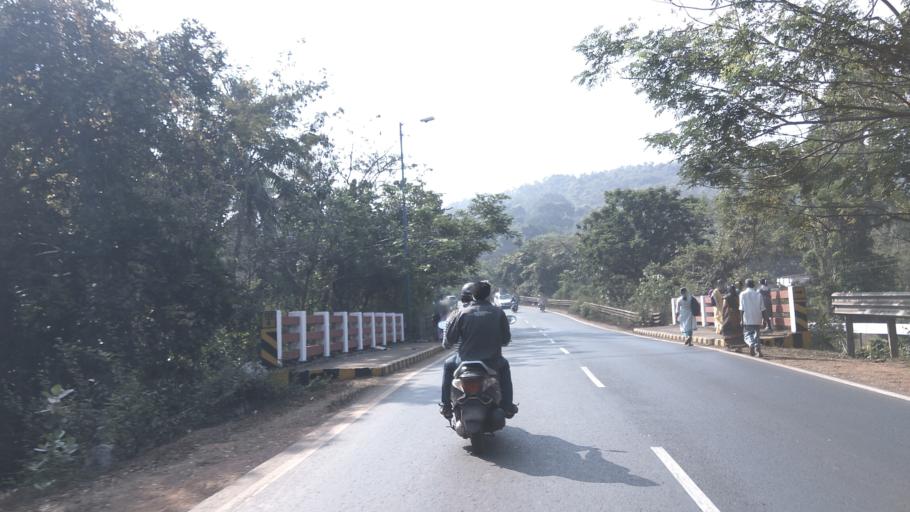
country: IN
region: Goa
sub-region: North Goa
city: Bandora
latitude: 15.4386
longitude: 73.9768
